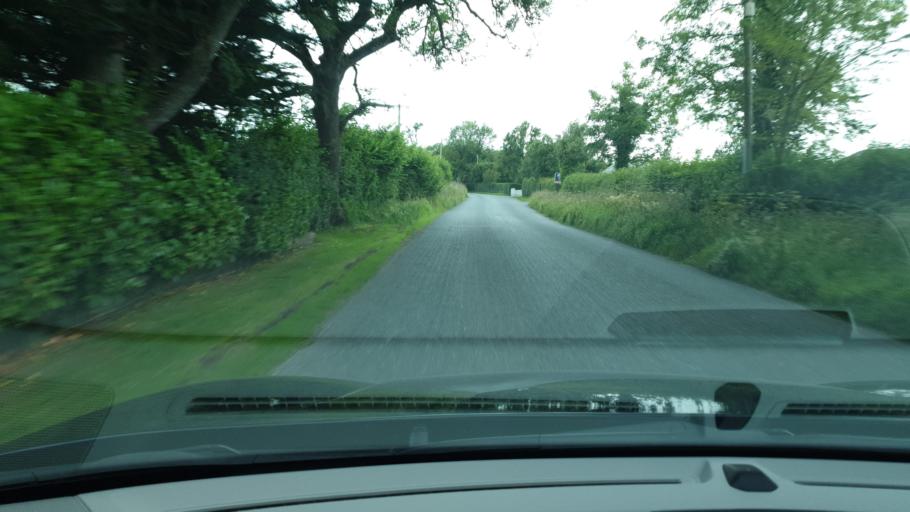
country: IE
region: Leinster
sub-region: An Mhi
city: Ashbourne
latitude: 53.5328
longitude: -6.4282
